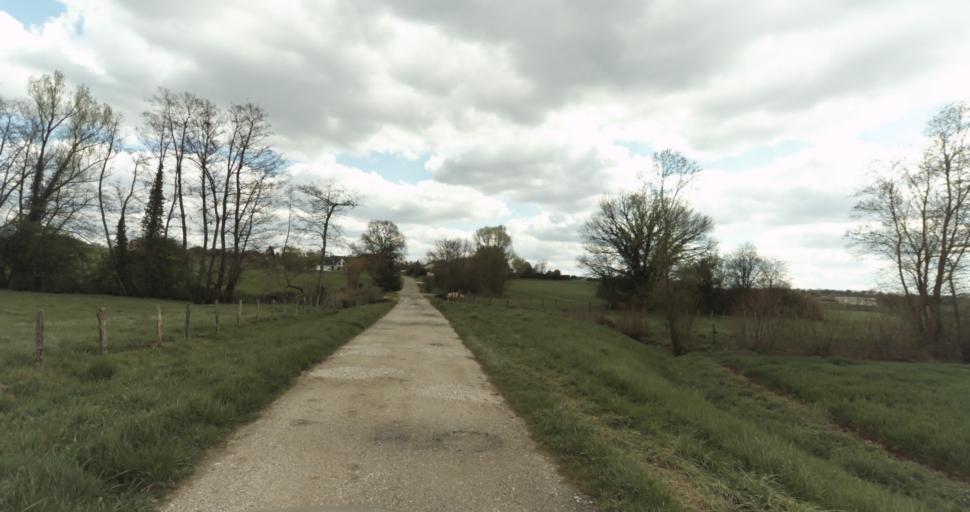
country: FR
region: Franche-Comte
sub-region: Departement du Jura
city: Champvans
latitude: 47.1482
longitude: 5.4269
